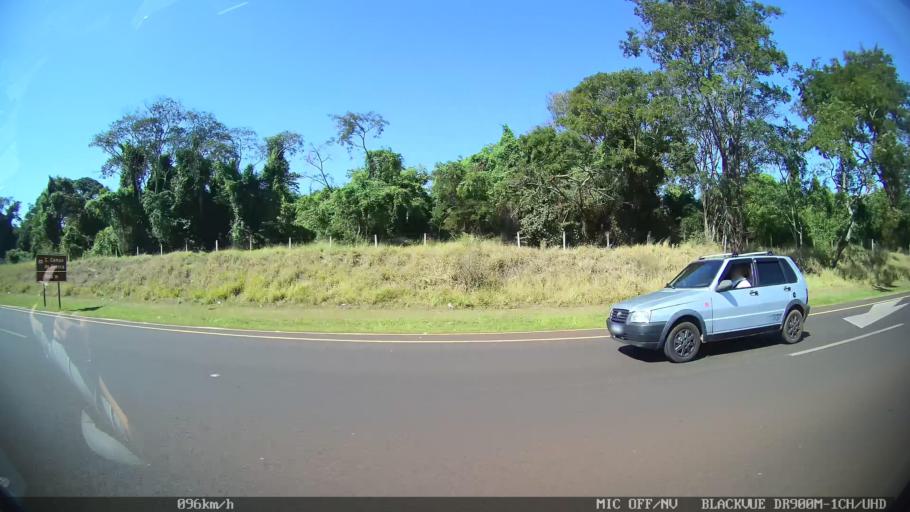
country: BR
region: Sao Paulo
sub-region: Franca
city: Franca
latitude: -20.6523
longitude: -47.4873
